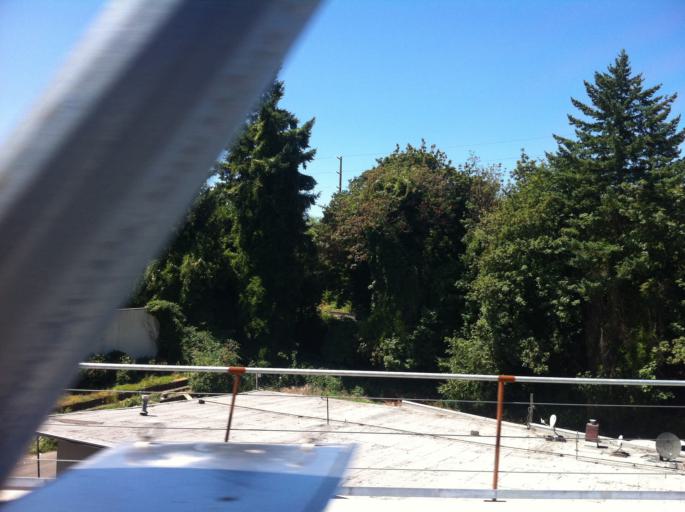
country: US
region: Oregon
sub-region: Clackamas County
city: Milwaukie
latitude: 45.4381
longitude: -122.6408
